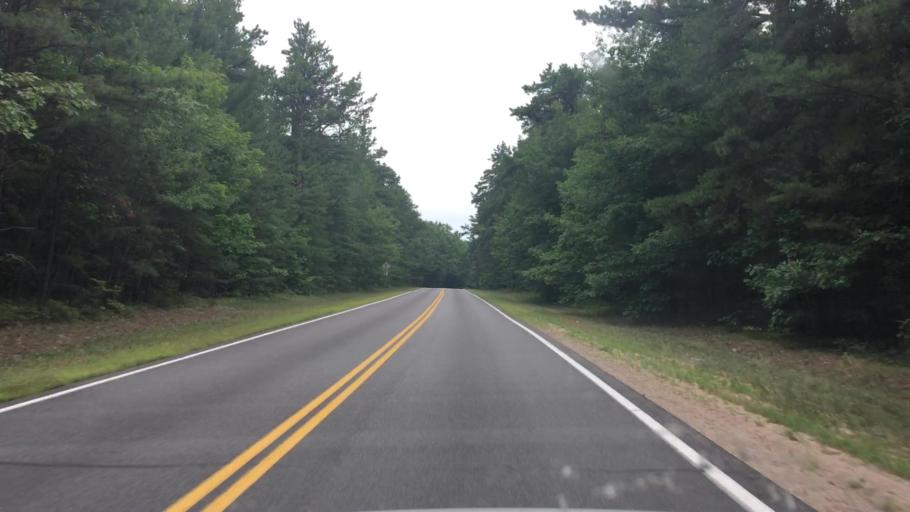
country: US
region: New York
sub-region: Clinton County
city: Morrisonville
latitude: 44.6201
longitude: -73.6192
